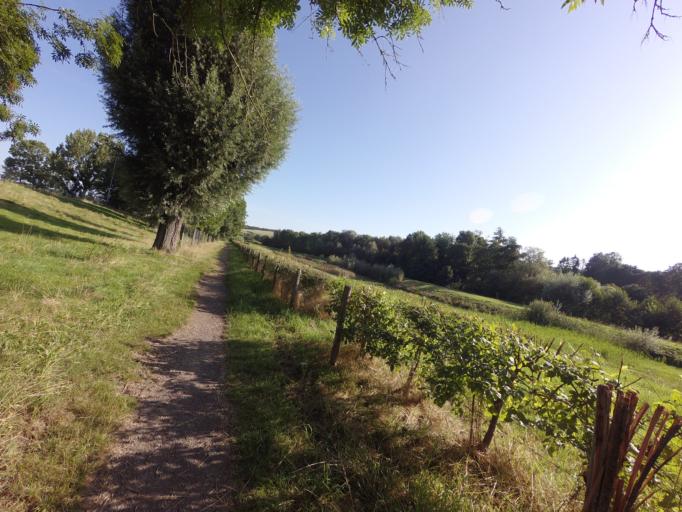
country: NL
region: Limburg
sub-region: Gemeente Vaals
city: Vaals
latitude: 50.7806
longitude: 5.9977
